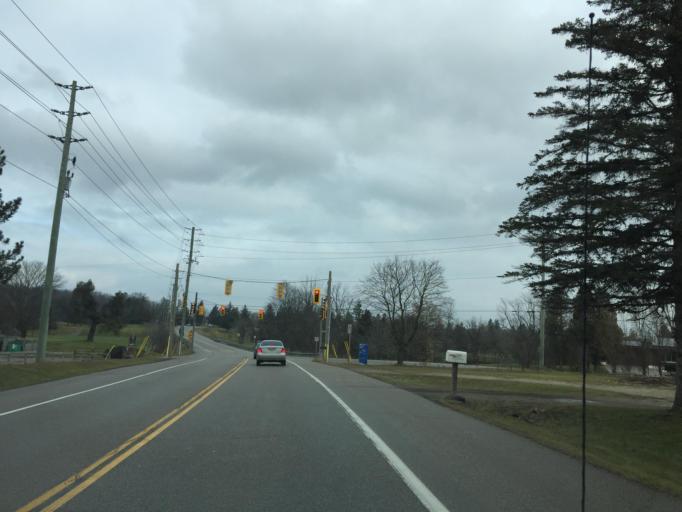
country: CA
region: Ontario
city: Cambridge
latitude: 43.4614
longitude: -80.3406
